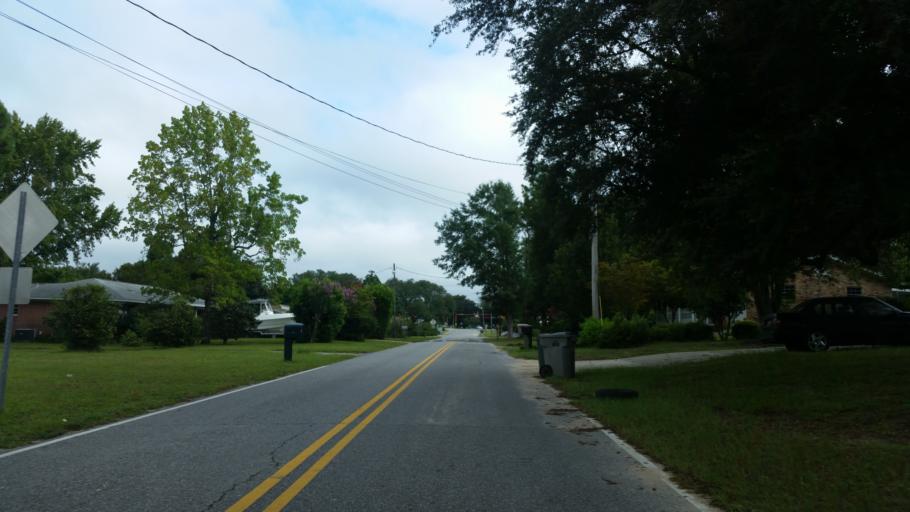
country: US
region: Florida
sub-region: Escambia County
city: Bellview
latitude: 30.4579
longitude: -87.2907
